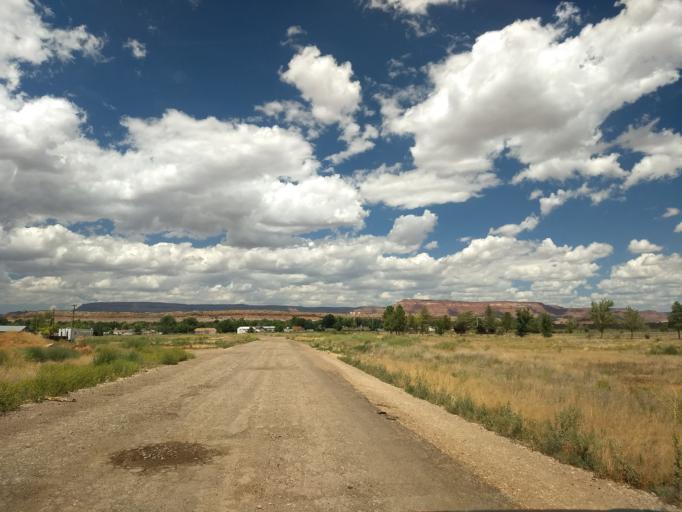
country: US
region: Arizona
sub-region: Coconino County
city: Fredonia
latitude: 36.9440
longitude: -112.5138
